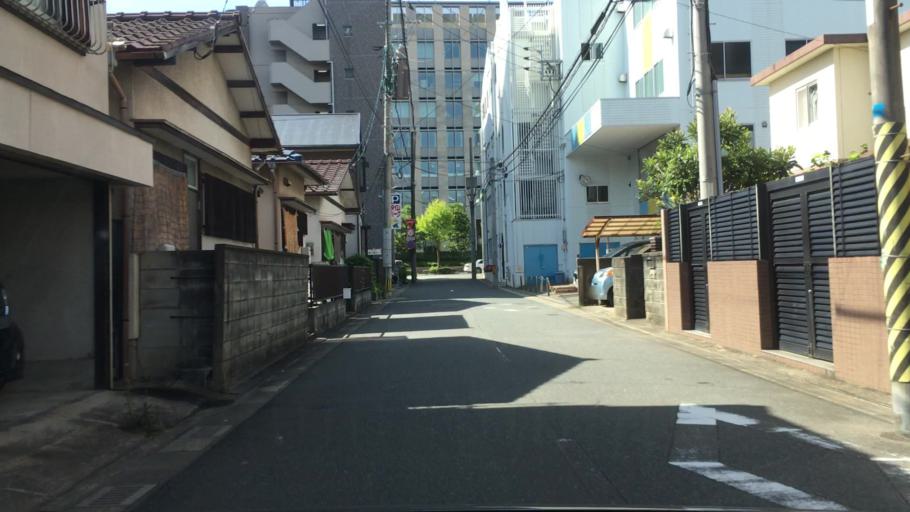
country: JP
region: Fukuoka
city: Fukuoka-shi
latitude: 33.5738
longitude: 130.3669
